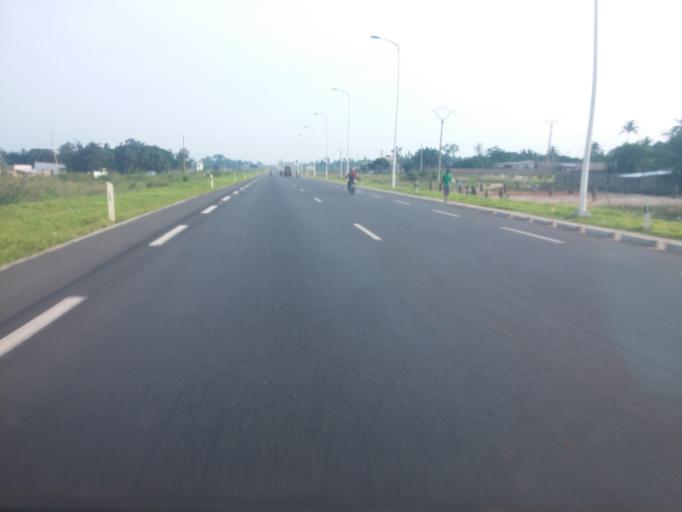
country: TG
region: Maritime
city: Tsevie
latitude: 6.3296
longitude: 1.2183
